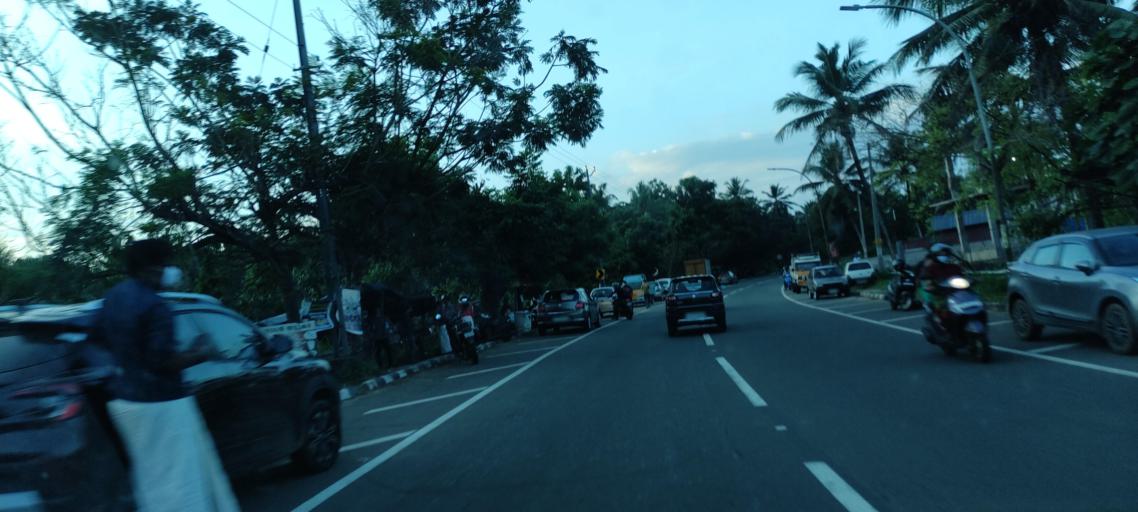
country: IN
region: Kerala
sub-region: Pattanamtitta
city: Adur
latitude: 9.1575
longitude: 76.7236
